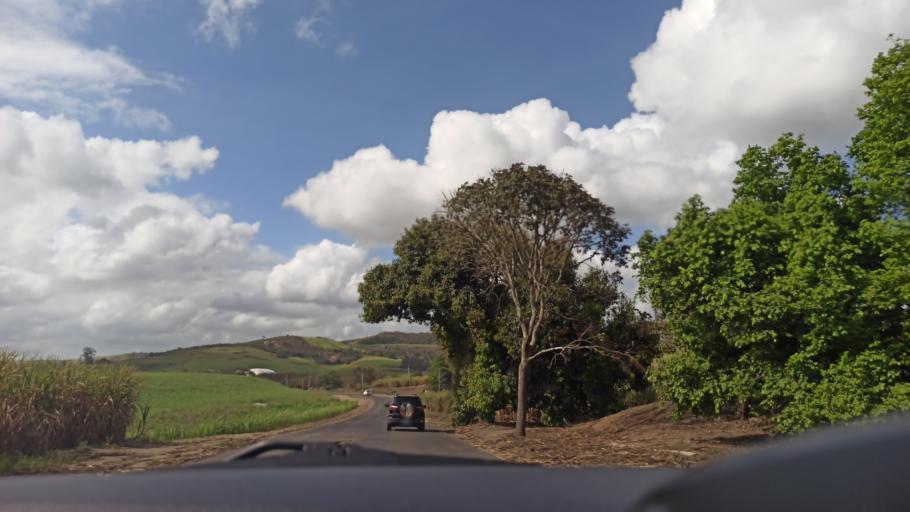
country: BR
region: Paraiba
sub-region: Juripiranga
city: Juripiranga
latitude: -7.4102
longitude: -35.2610
